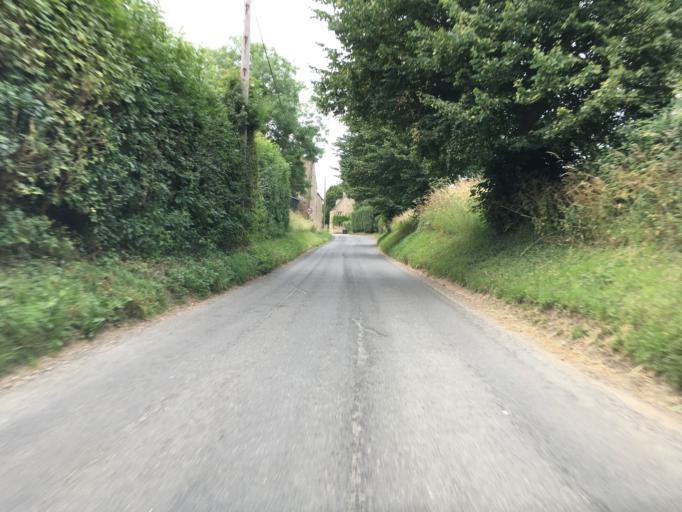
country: GB
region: England
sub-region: Oxfordshire
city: Shipton under Wychwood
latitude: 51.8968
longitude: -1.6378
